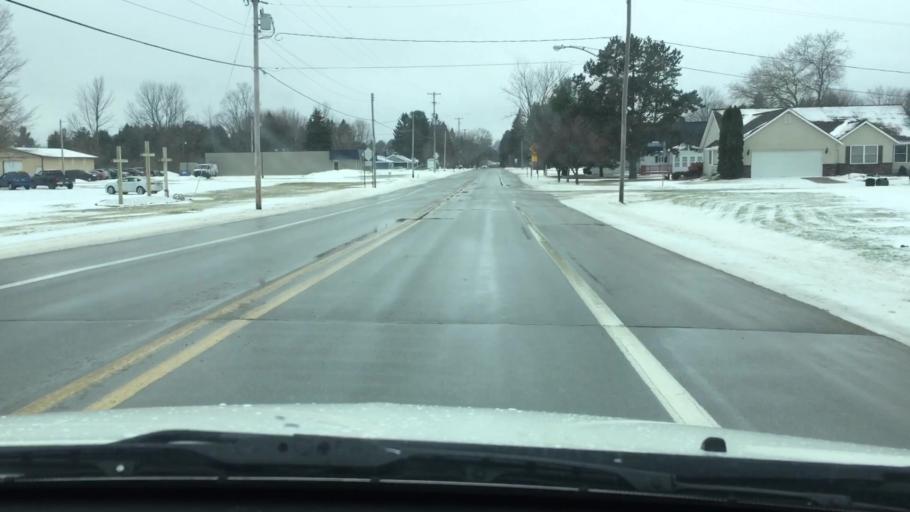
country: US
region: Michigan
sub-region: Wexford County
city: Cadillac
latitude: 44.2339
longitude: -85.4151
